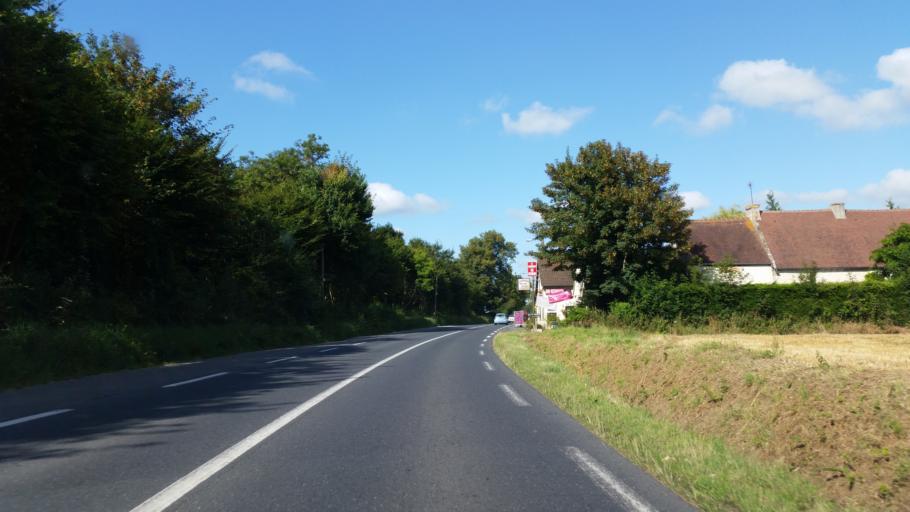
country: FR
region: Lower Normandy
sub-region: Departement du Calvados
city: Bavent
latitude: 49.2396
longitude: -0.1885
